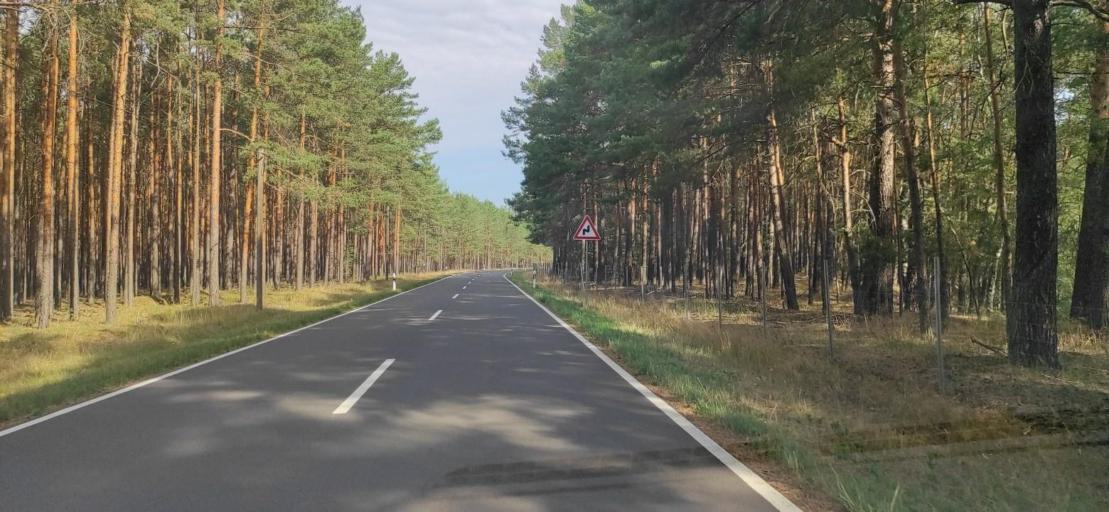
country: PL
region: Lubusz
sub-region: Powiat zarski
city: Trzebiel
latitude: 51.6230
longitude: 14.7529
